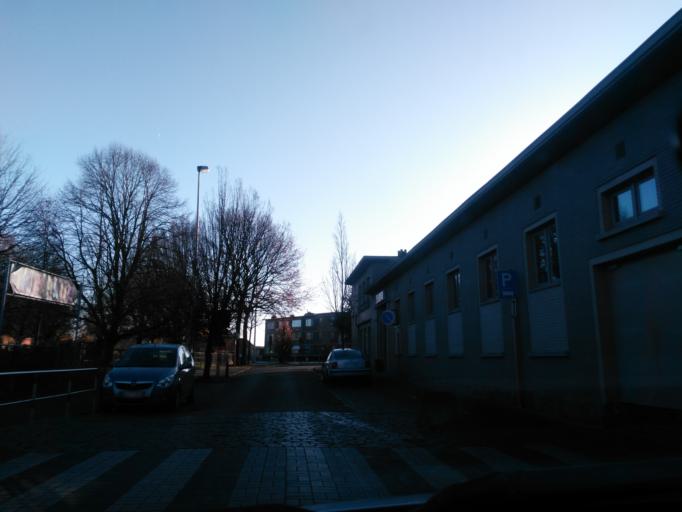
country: BE
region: Flanders
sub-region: Provincie Oost-Vlaanderen
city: Beveren
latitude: 51.2208
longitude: 4.2868
